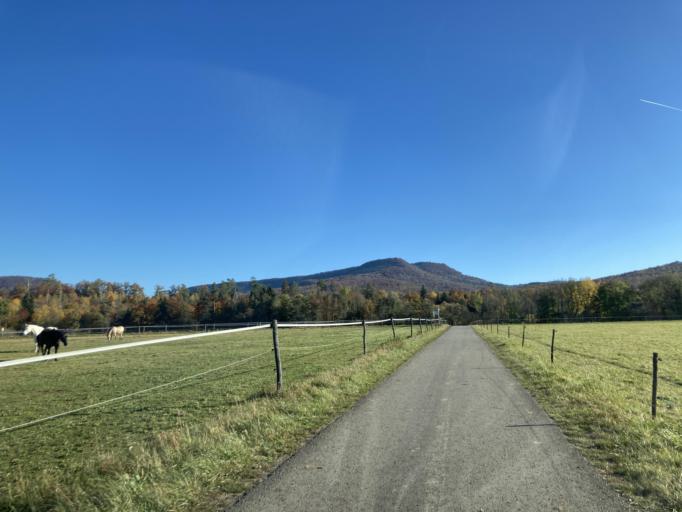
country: DE
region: Baden-Wuerttemberg
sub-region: Tuebingen Region
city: Ofterdingen
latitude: 48.3920
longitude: 9.0131
